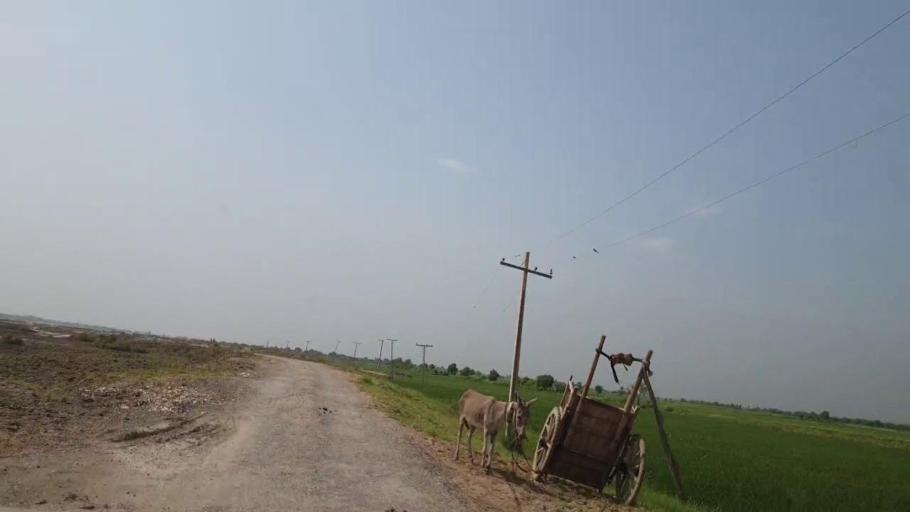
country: PK
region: Sindh
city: Dokri
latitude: 27.4256
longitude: 68.2040
